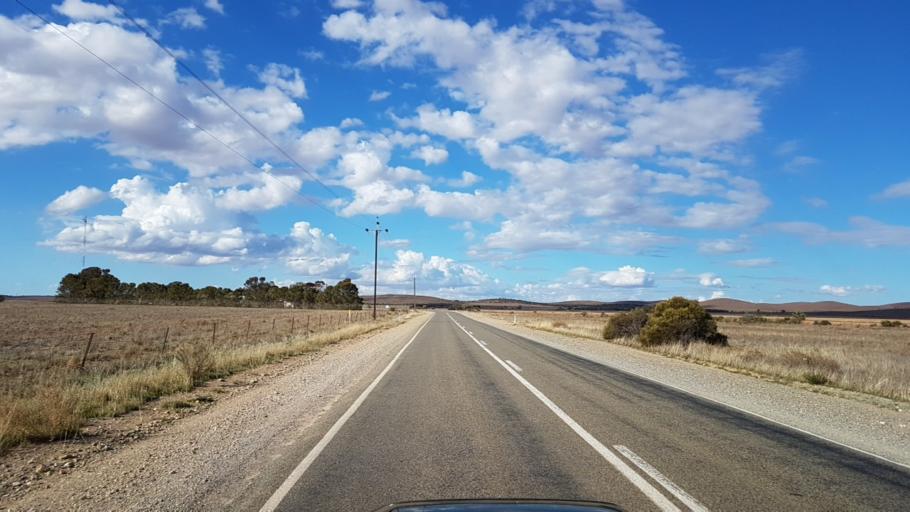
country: AU
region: South Australia
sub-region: Peterborough
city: Peterborough
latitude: -32.9692
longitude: 138.8650
